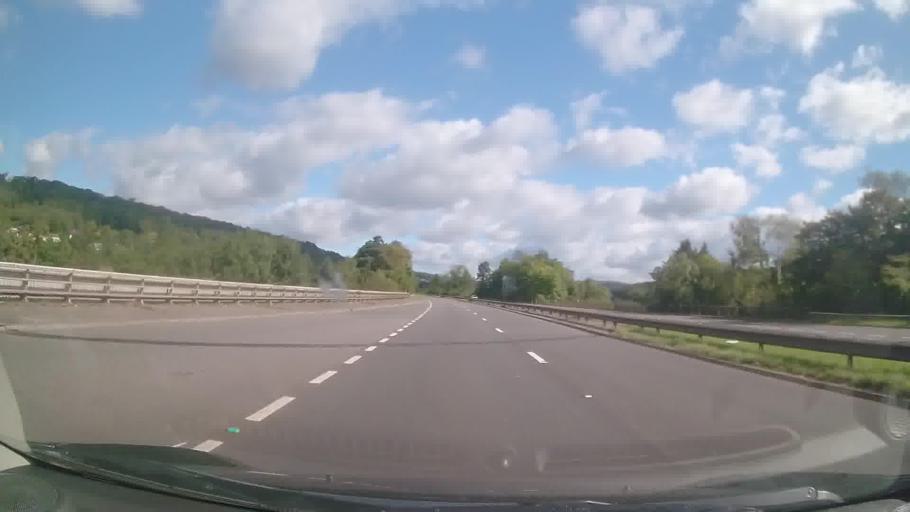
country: GB
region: Wales
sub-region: Neath Port Talbot
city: Glyn-neath
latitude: 51.7475
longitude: -3.6115
